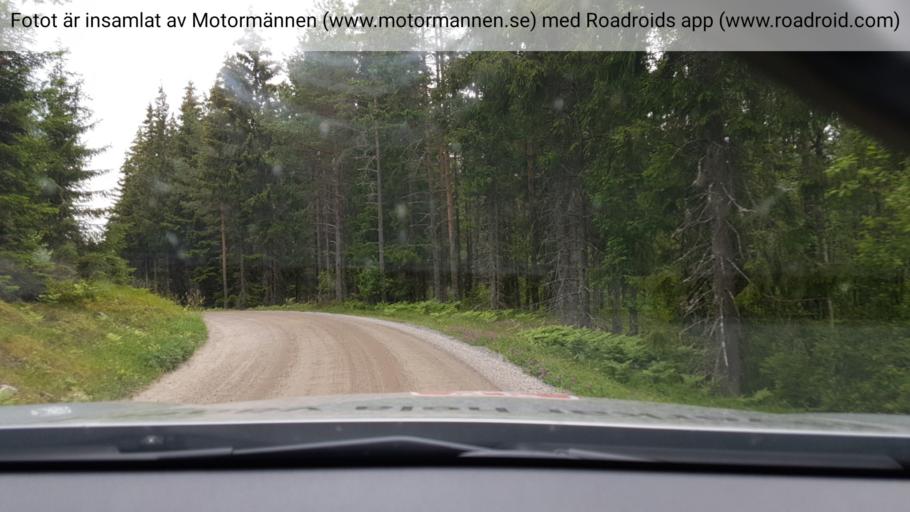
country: SE
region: Joenkoeping
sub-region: Mullsjo Kommun
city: Mullsjoe
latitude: 57.9101
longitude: 13.8035
